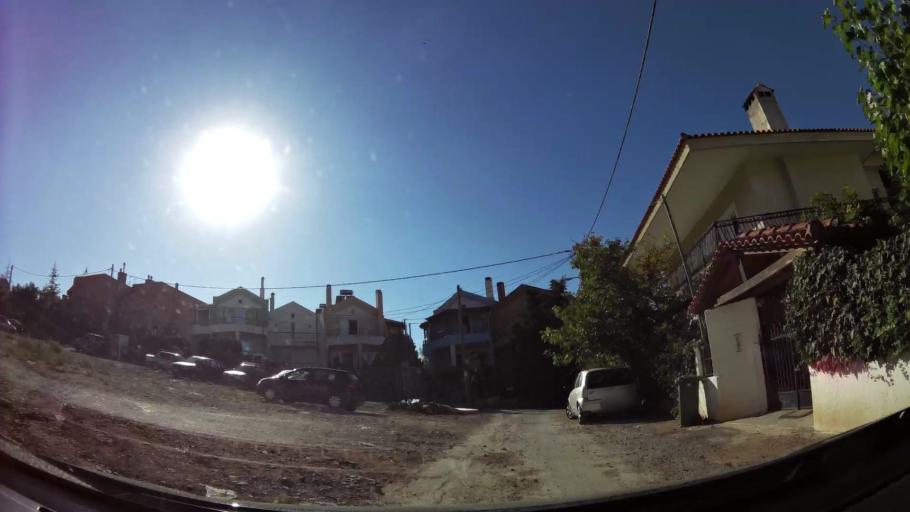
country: GR
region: Attica
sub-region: Nomarchia Anatolikis Attikis
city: Anoixi
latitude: 38.1357
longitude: 23.8649
